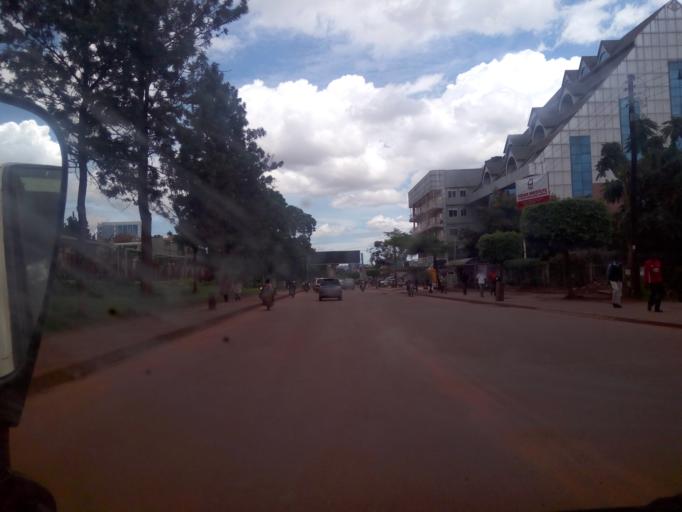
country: UG
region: Central Region
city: Kampala Central Division
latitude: 0.3244
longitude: 32.5741
